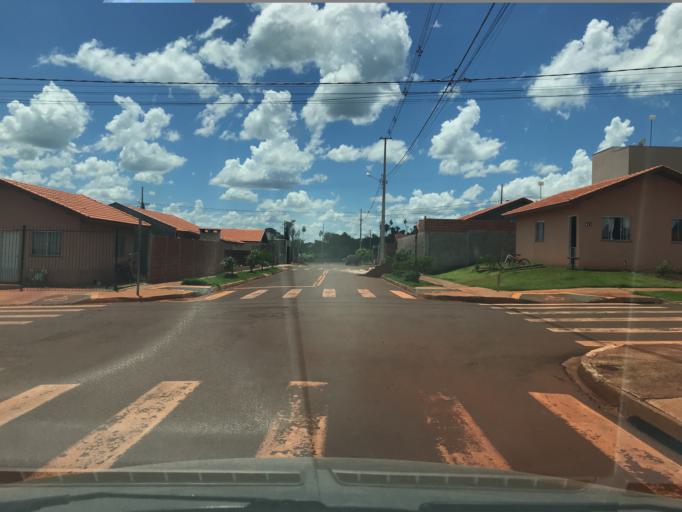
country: BR
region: Parana
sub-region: Palotina
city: Palotina
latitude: -24.2659
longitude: -53.8475
